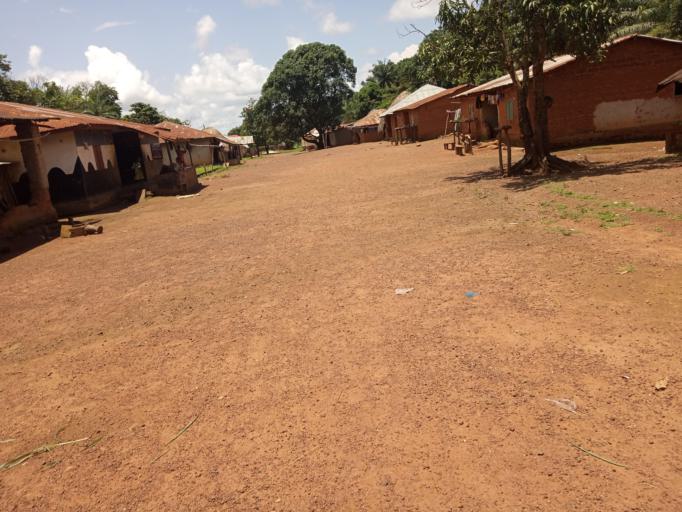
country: SL
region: Northern Province
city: Kamakwie
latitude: 9.4682
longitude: -12.2501
